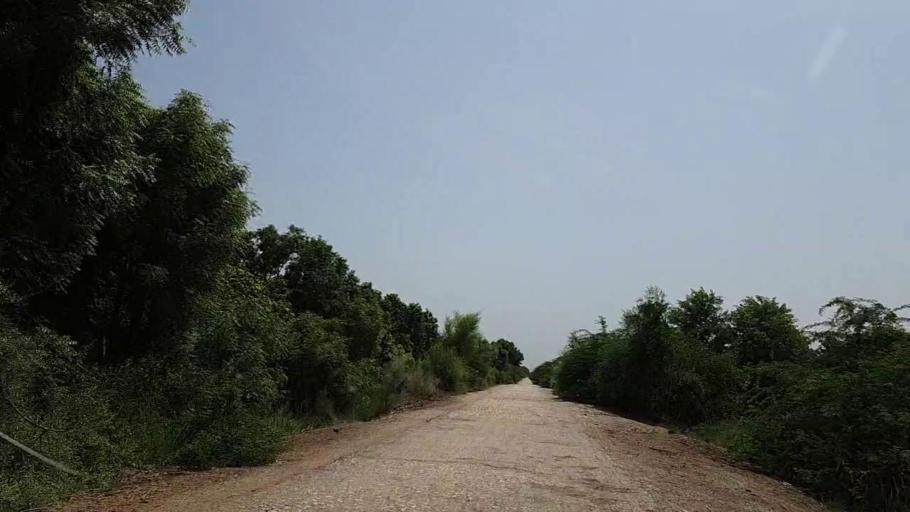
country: PK
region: Sindh
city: Kandiaro
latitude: 27.0360
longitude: 68.1264
